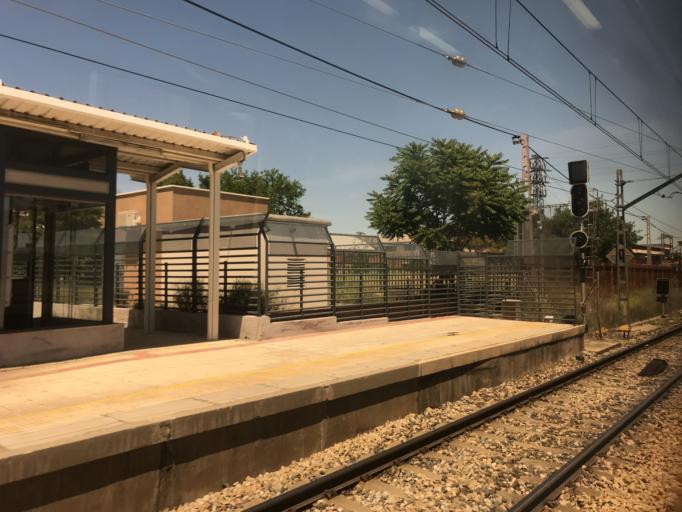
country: ES
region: Madrid
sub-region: Provincia de Madrid
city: Villaverde
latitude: 40.3319
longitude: -3.6988
